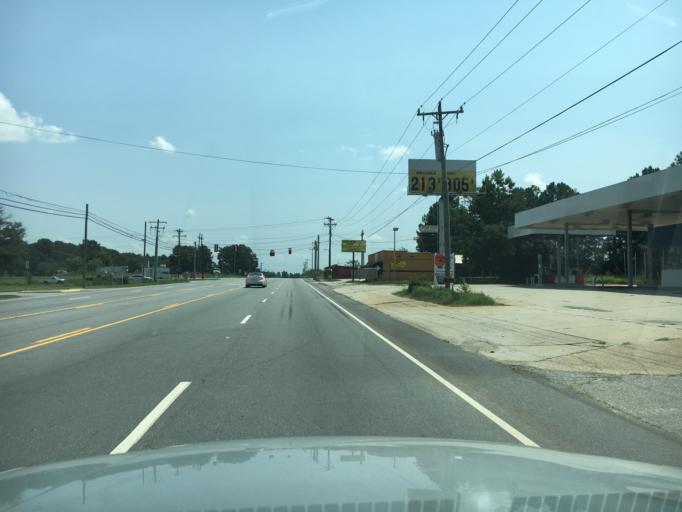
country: US
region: South Carolina
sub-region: Anderson County
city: Pendleton
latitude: 34.6316
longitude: -82.7826
